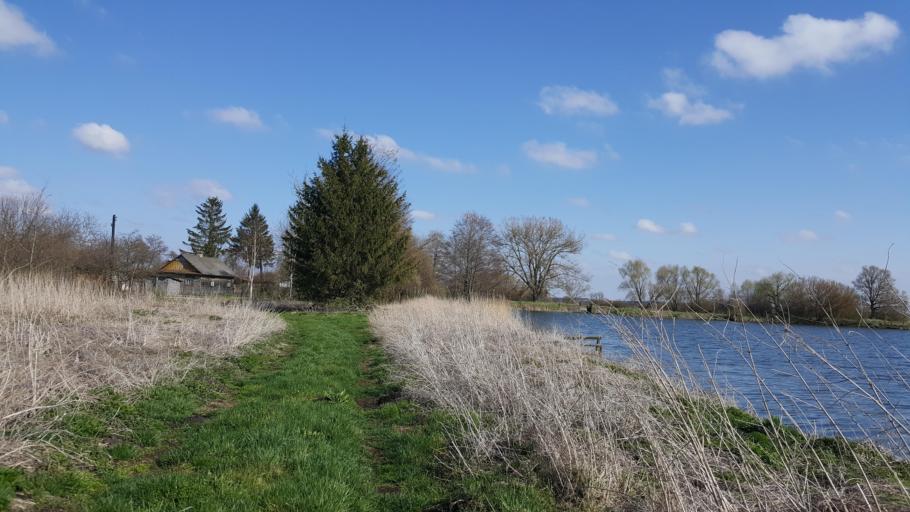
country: BY
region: Brest
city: Kamyanyets
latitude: 52.4070
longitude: 23.7793
